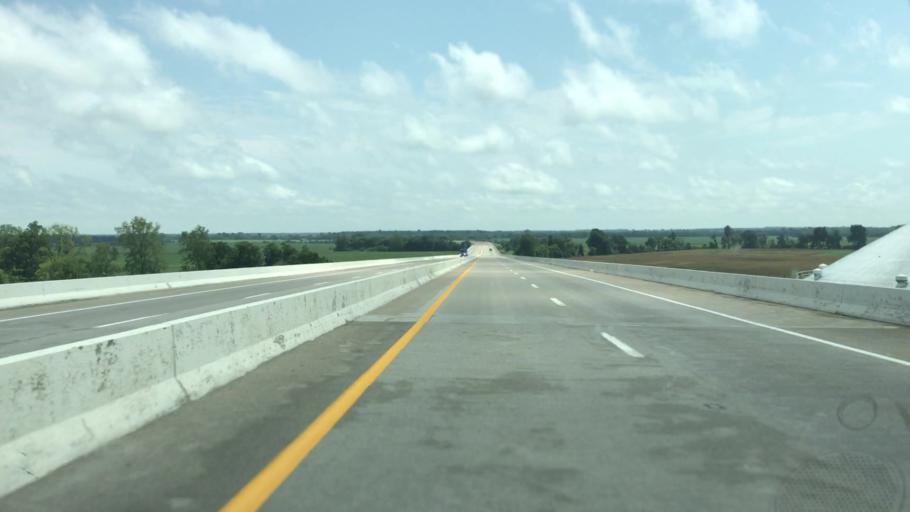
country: US
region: Missouri
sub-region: Pemiscot County
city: Caruthersville
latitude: 36.1116
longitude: -89.6112
